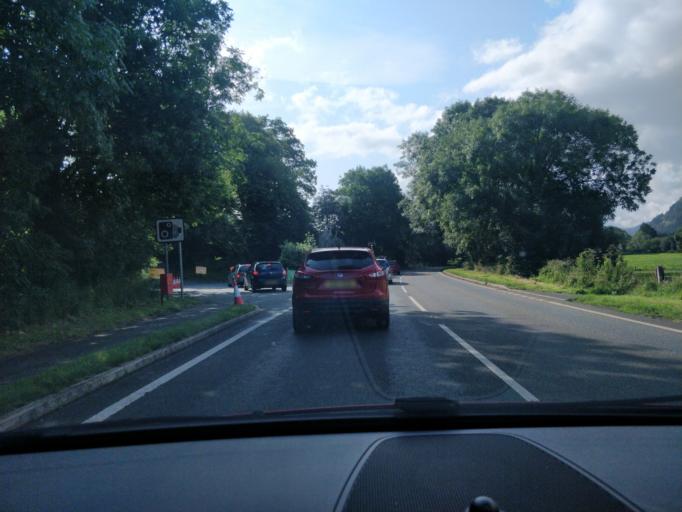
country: GB
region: Wales
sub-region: Conwy
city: Llanrwst
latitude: 53.1471
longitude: -3.8035
